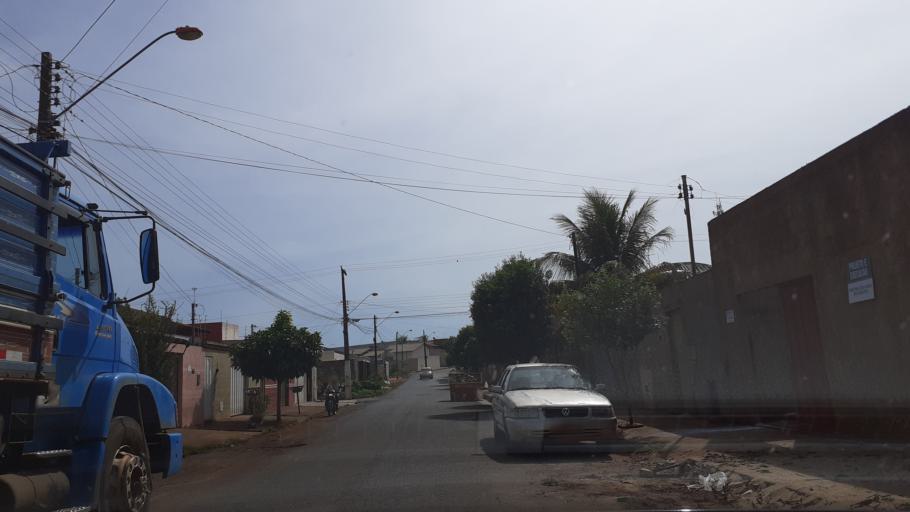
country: BR
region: Goias
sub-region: Itumbiara
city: Itumbiara
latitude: -18.4214
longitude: -49.2324
